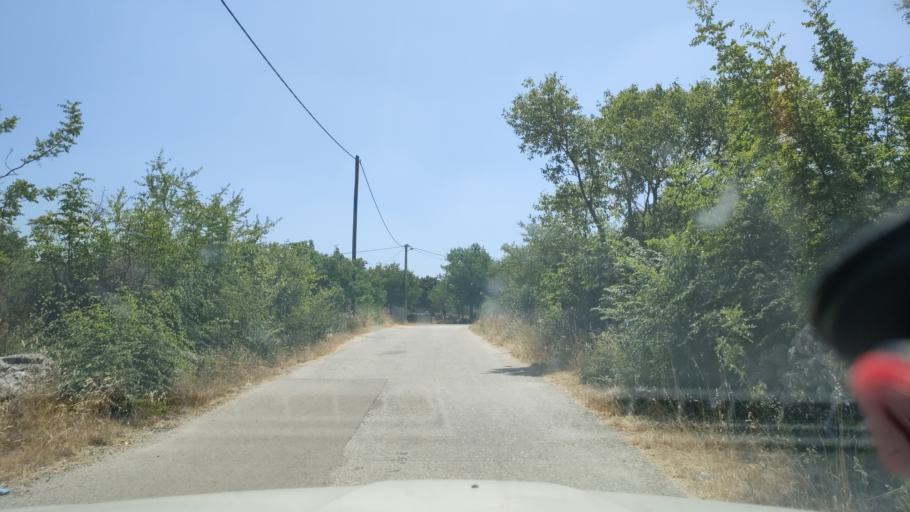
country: HR
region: Sibensko-Kniniska
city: Kistanje
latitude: 43.9508
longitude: 15.8827
